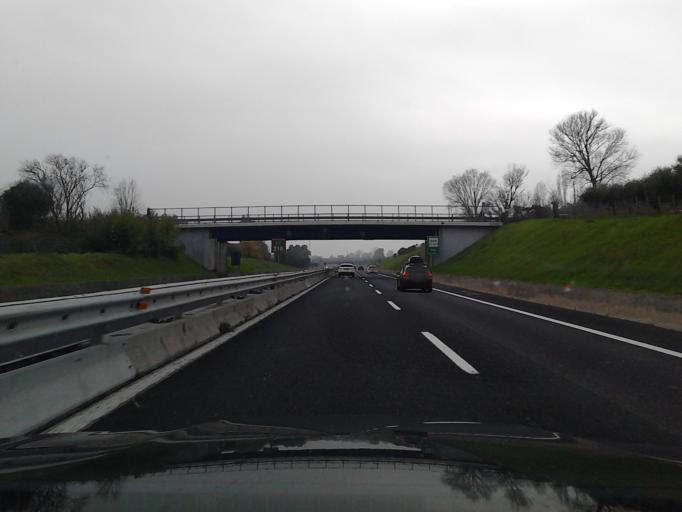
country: IT
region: Abruzzo
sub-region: Provincia di Pescara
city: San Martino Bassa
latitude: 42.5170
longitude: 14.1314
